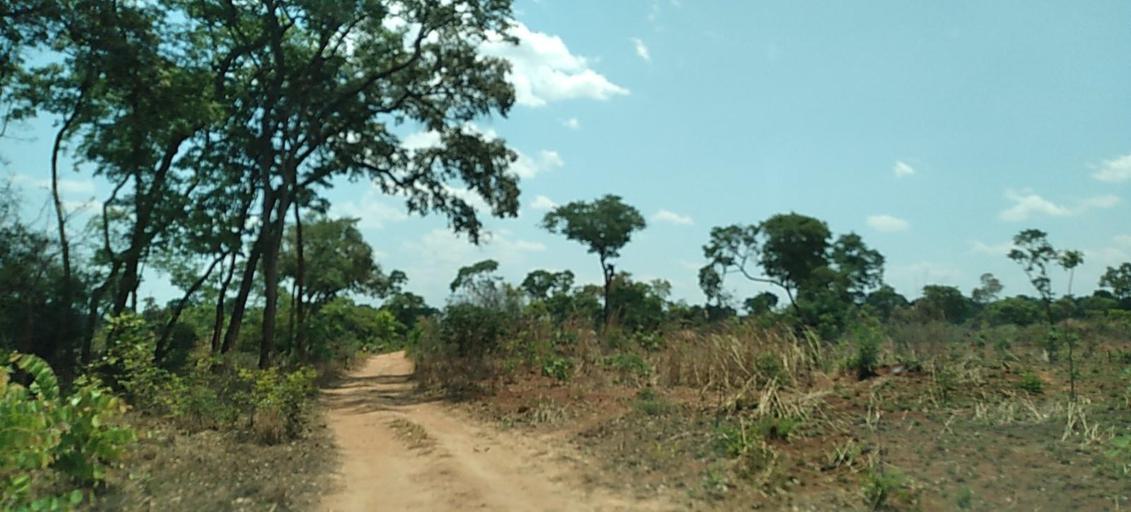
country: ZM
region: Central
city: Kapiri Mposhi
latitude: -13.6311
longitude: 28.7672
